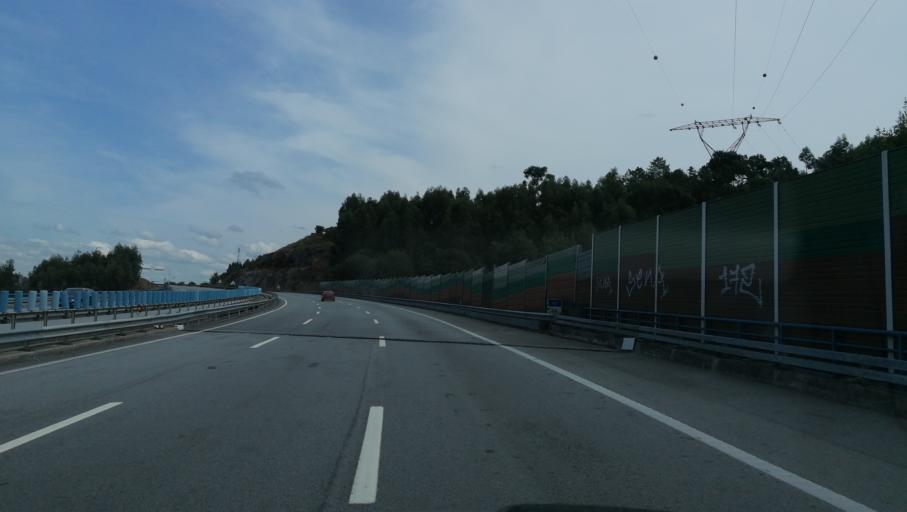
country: PT
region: Braga
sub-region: Guimaraes
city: Serzedelo
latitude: 41.4096
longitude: -8.3677
